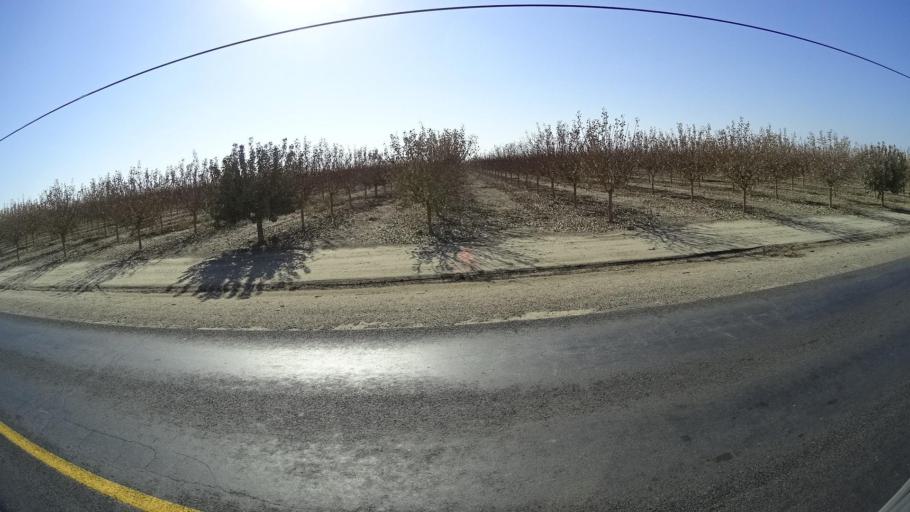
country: US
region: California
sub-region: Kern County
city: Delano
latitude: 35.7177
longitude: -119.3496
